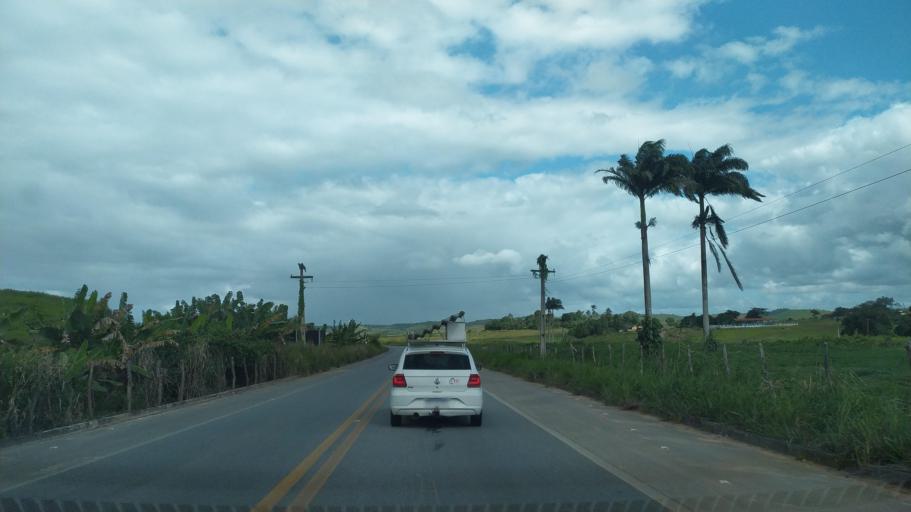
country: BR
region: Alagoas
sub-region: Murici
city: Murici
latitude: -9.2893
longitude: -35.9627
